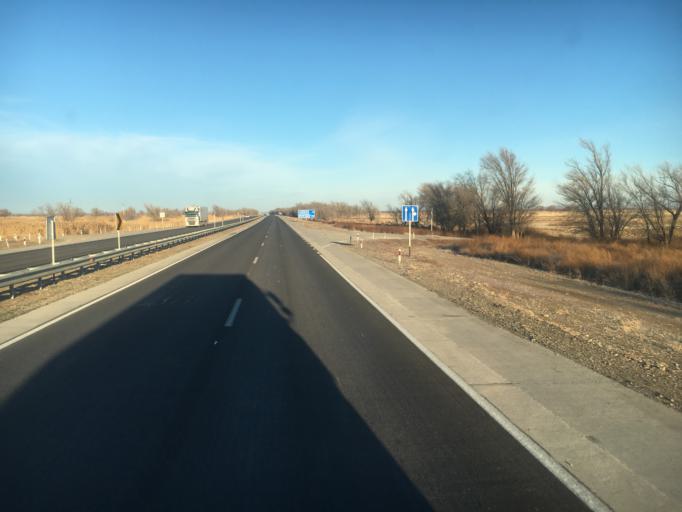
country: KZ
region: Ongtustik Qazaqstan
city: Bayaldyr
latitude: 43.0935
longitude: 68.6369
